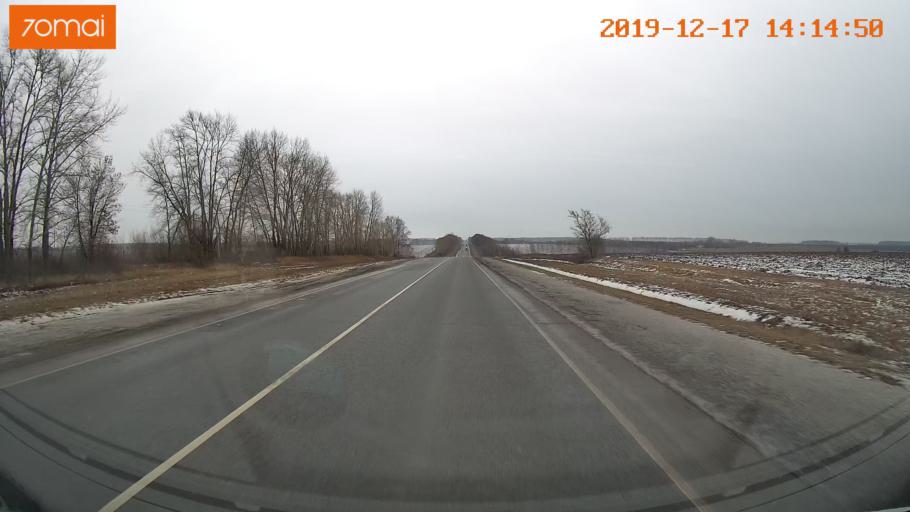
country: RU
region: Rjazan
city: Bagramovo
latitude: 54.4999
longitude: 39.4819
